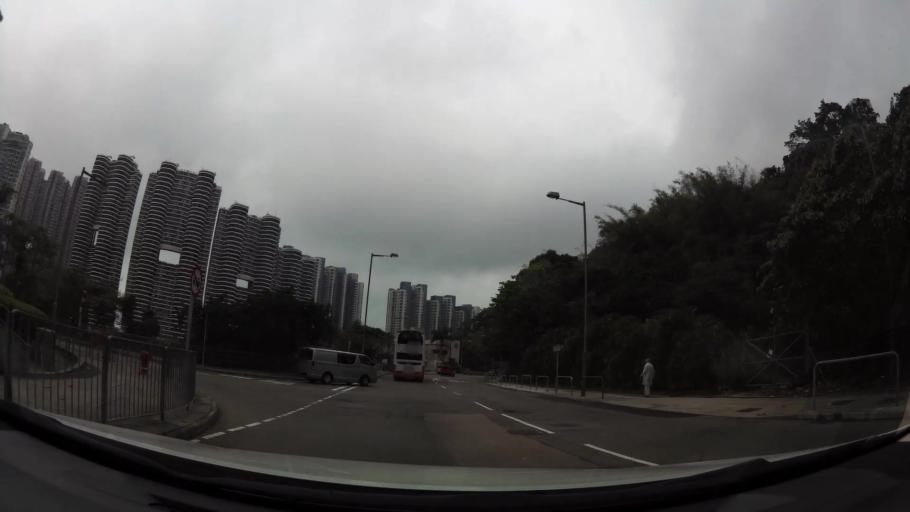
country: HK
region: Central and Western
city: Central
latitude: 22.2547
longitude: 114.1367
